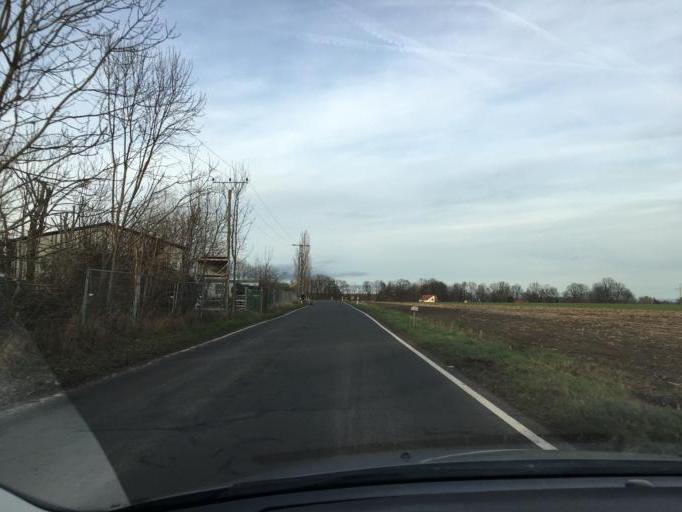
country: DE
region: Saxony
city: Belgershain
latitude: 51.2115
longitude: 12.5242
